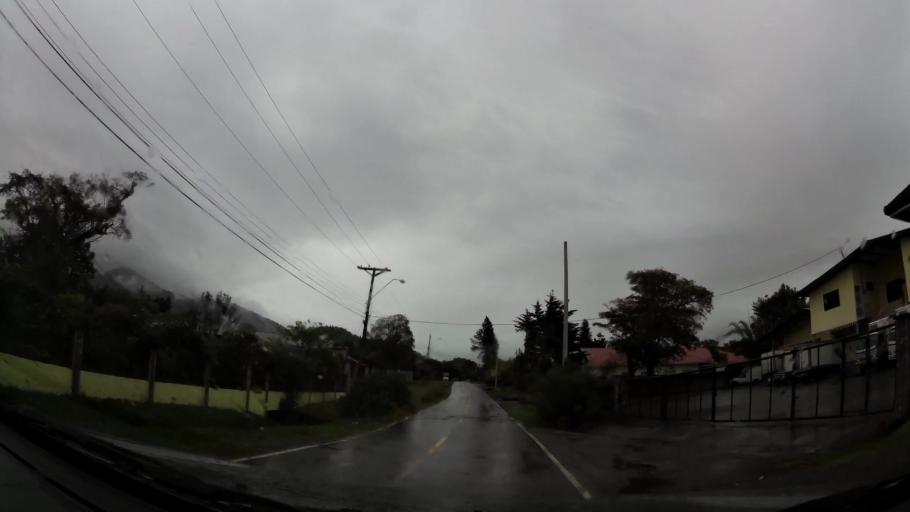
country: PA
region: Chiriqui
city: Volcan
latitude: 8.7892
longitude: -82.6529
